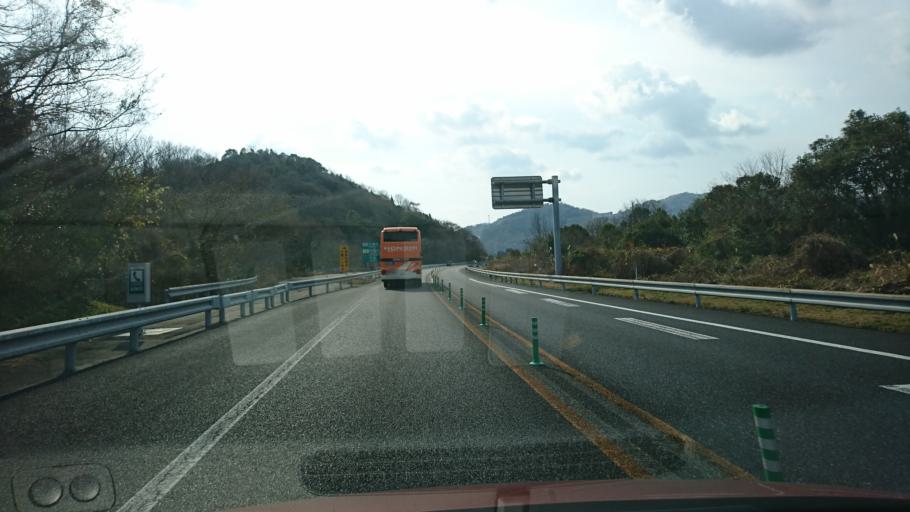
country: JP
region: Hiroshima
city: Innoshima
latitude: 34.2009
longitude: 133.0790
